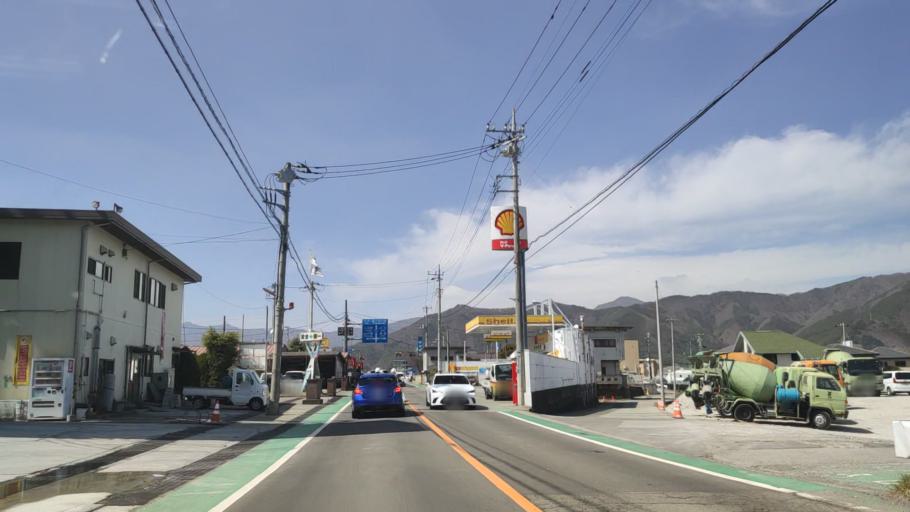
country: JP
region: Yamanashi
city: Fujikawaguchiko
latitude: 35.4802
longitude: 138.8118
